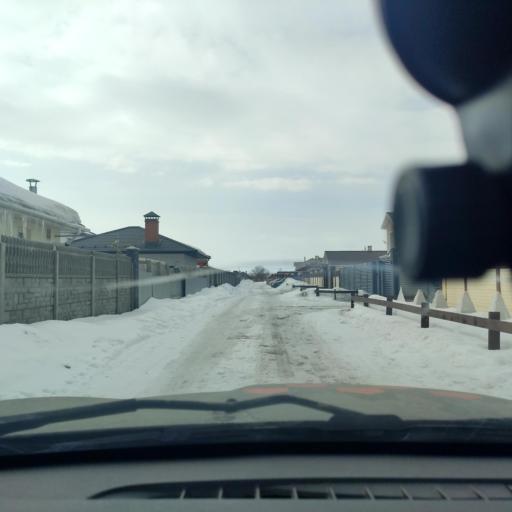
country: RU
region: Samara
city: Podstepki
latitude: 53.5112
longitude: 49.1750
